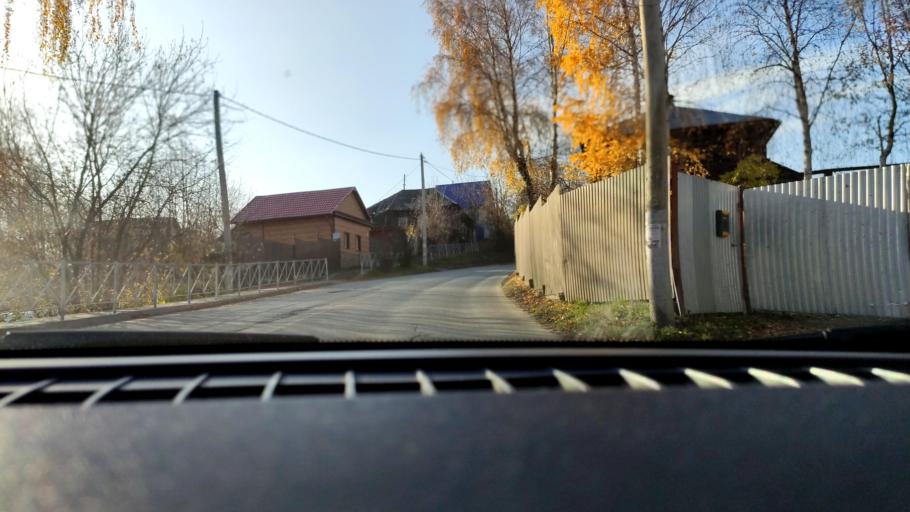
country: RU
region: Perm
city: Perm
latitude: 58.0275
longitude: 56.3149
